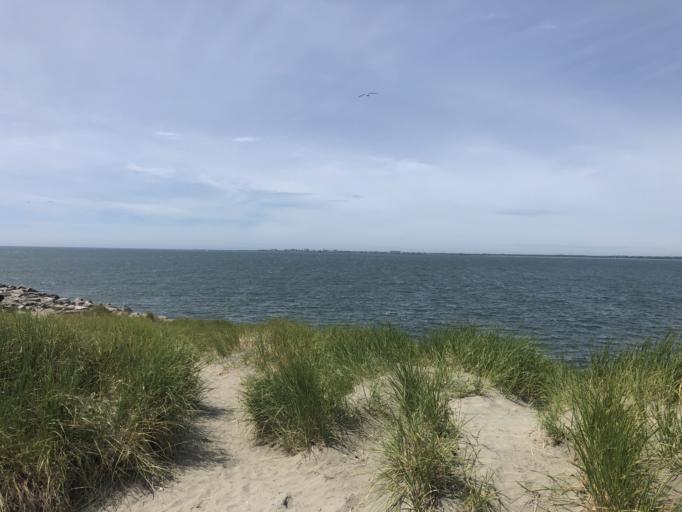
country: US
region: Washington
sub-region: Grays Harbor County
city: Westport
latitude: 46.9049
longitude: -124.1324
